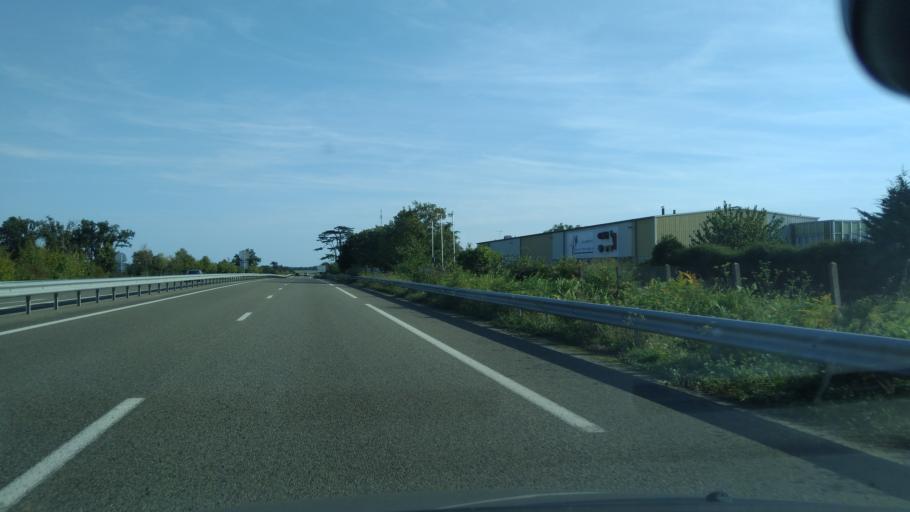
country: FR
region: Pays de la Loire
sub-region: Departement de la Mayenne
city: Entrammes
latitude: 48.0128
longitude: -0.7290
